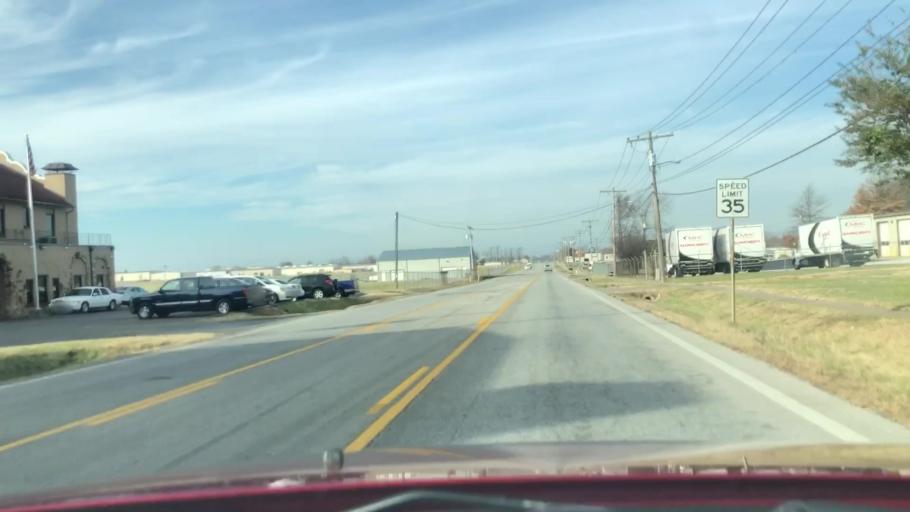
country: US
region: Missouri
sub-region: Greene County
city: Springfield
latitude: 37.2252
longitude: -93.2496
